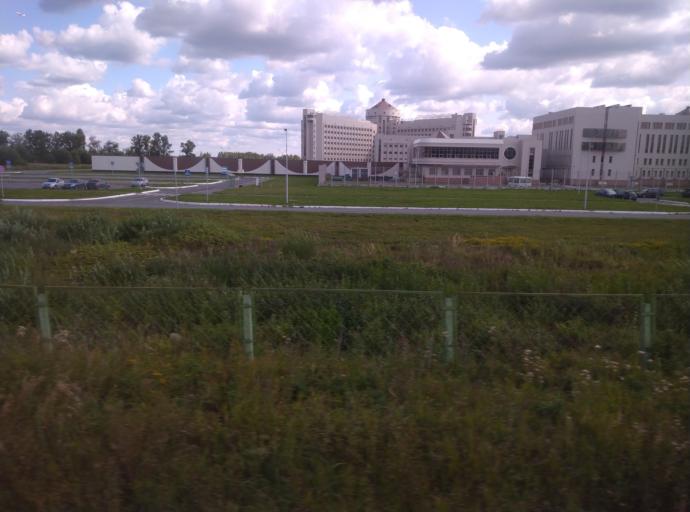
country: RU
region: St.-Petersburg
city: Kolpino
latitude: 59.7391
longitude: 30.6274
